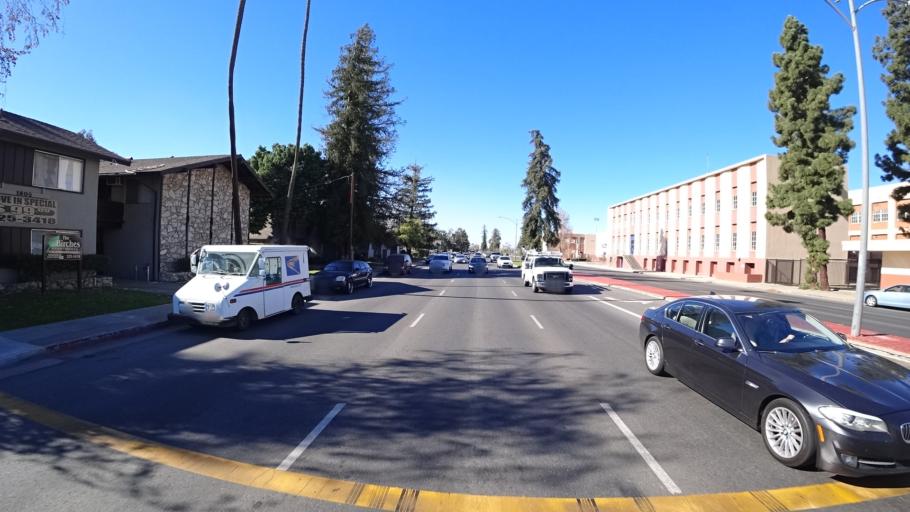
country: US
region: California
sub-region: Kern County
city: Bakersfield
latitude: 35.3684
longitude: -119.0226
